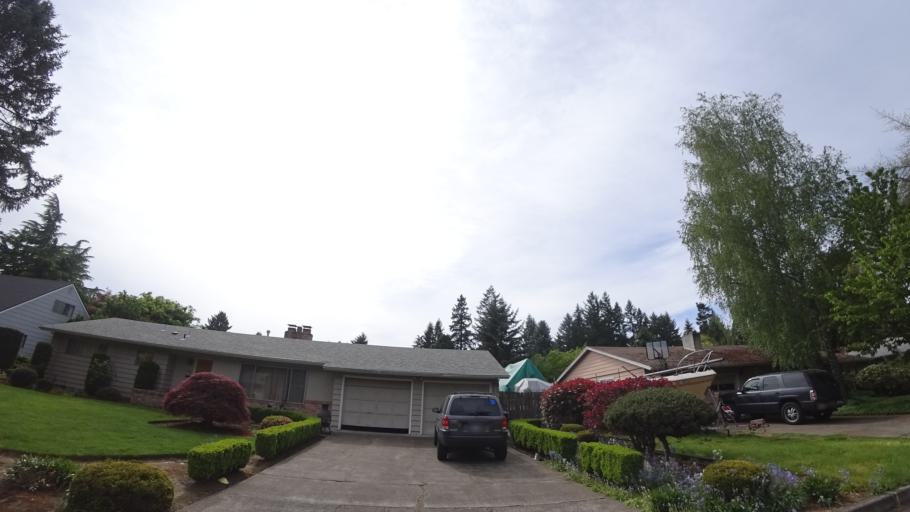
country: US
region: Oregon
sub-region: Washington County
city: Hillsboro
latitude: 45.5099
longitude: -122.9447
